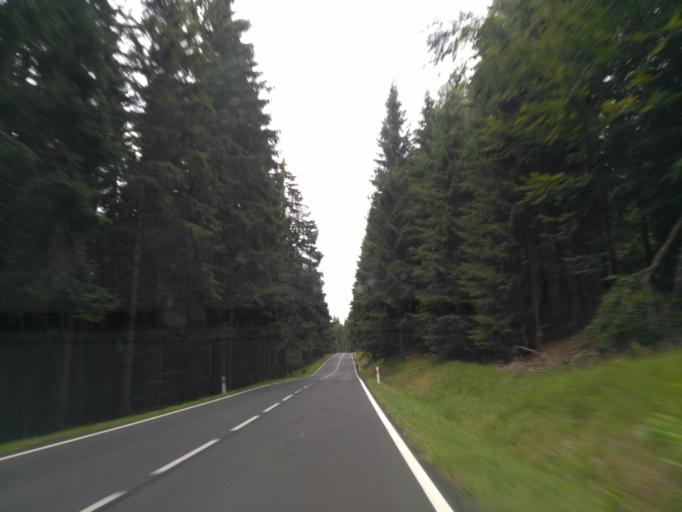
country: CZ
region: Karlovarsky
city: Merklin
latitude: 50.3814
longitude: 12.8823
